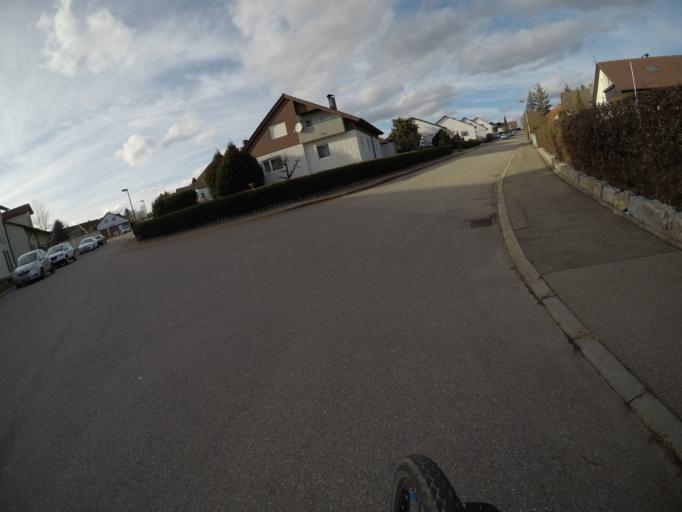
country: DE
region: Baden-Wuerttemberg
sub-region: Regierungsbezirk Stuttgart
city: Nufringen
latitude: 48.6221
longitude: 8.8822
